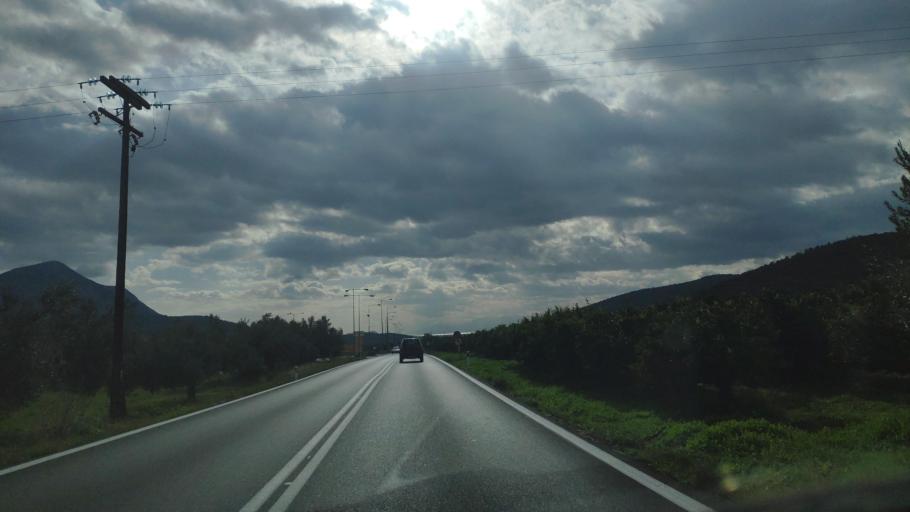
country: GR
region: Peloponnese
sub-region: Nomos Argolidos
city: Koutsopodi
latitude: 37.7564
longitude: 22.7326
